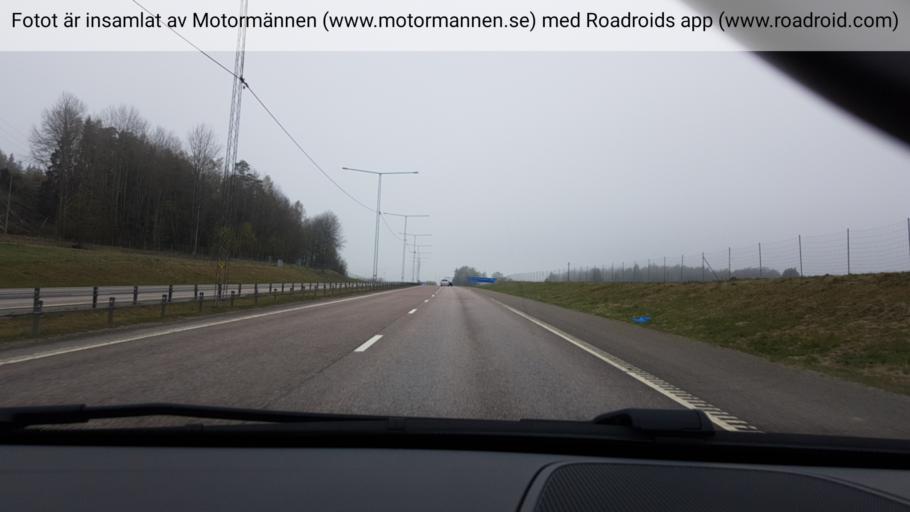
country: SE
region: Stockholm
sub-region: Haninge Kommun
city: Jordbro
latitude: 59.1286
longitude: 18.1403
